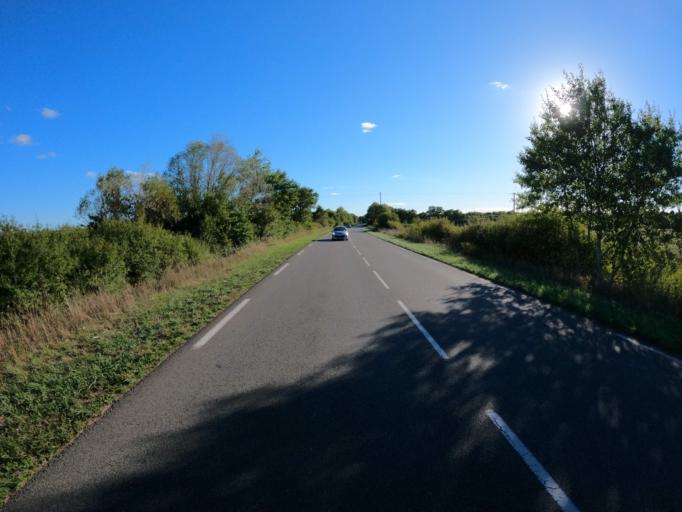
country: FR
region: Bourgogne
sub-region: Departement de Saone-et-Loire
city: Saint-Eusebe
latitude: 46.7366
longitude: 4.4438
